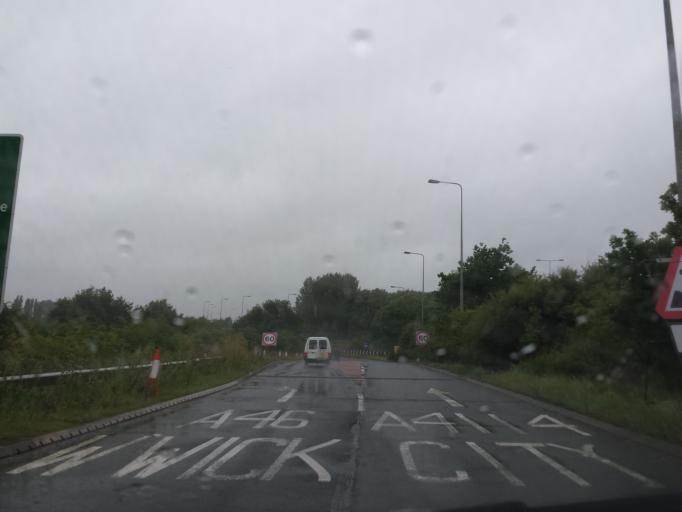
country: GB
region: England
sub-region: Coventry
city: Coventry
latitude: 52.3774
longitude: -1.4964
